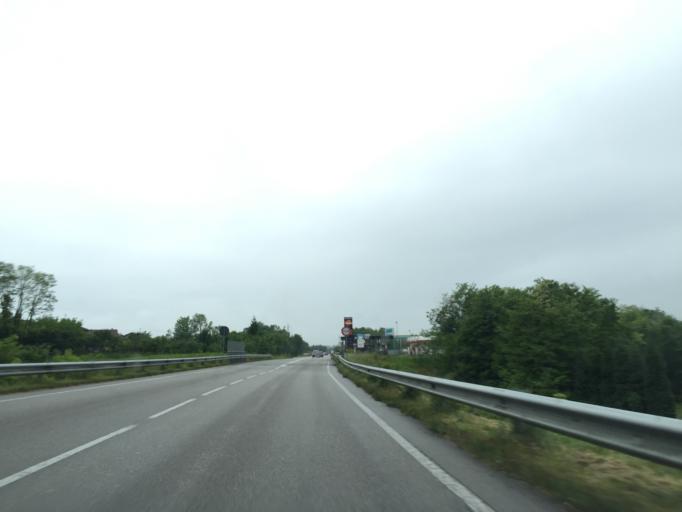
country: IT
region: Veneto
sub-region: Provincia di Belluno
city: Trichiana
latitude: 46.0844
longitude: 12.1455
